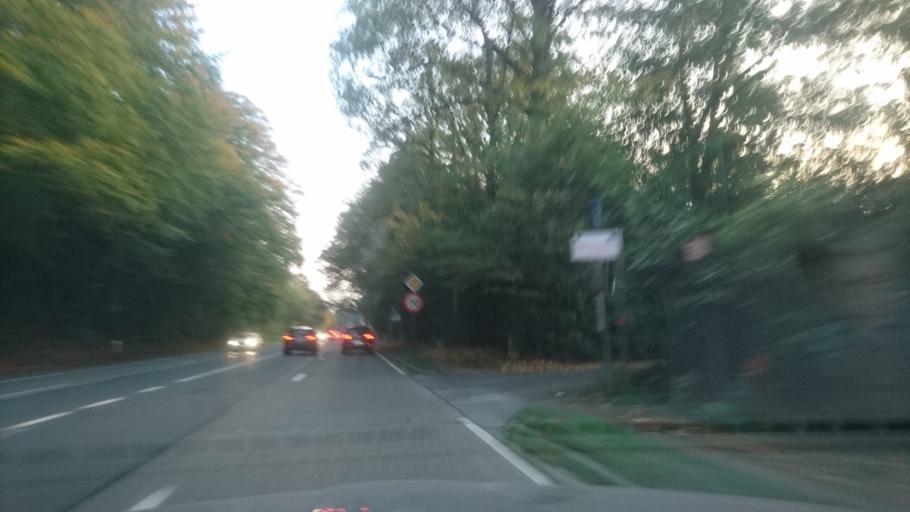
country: BE
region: Flanders
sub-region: Provincie Vlaams-Brabant
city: Sint-Genesius-Rode
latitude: 50.7675
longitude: 4.3826
